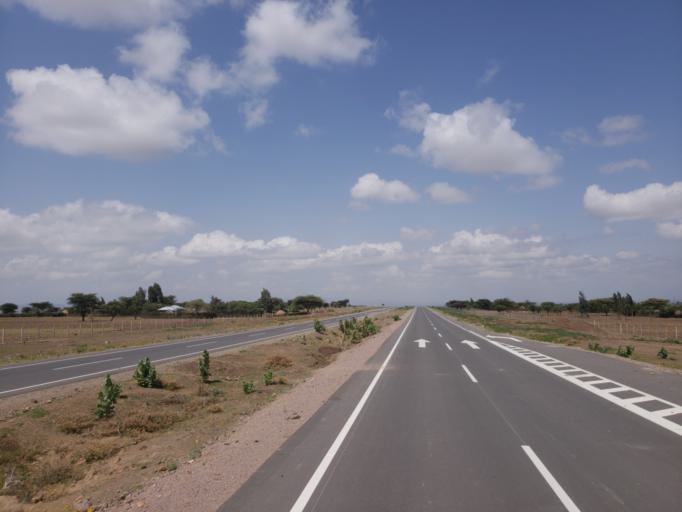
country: ET
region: Oromiya
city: Mojo
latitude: 8.5302
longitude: 39.0950
